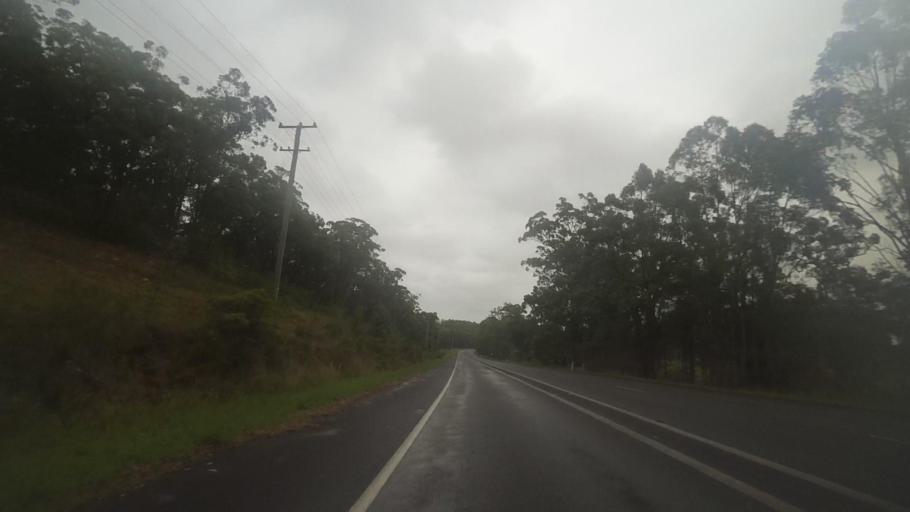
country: AU
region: New South Wales
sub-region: Port Stephens Shire
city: Port Stephens
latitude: -32.6450
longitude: 151.9829
